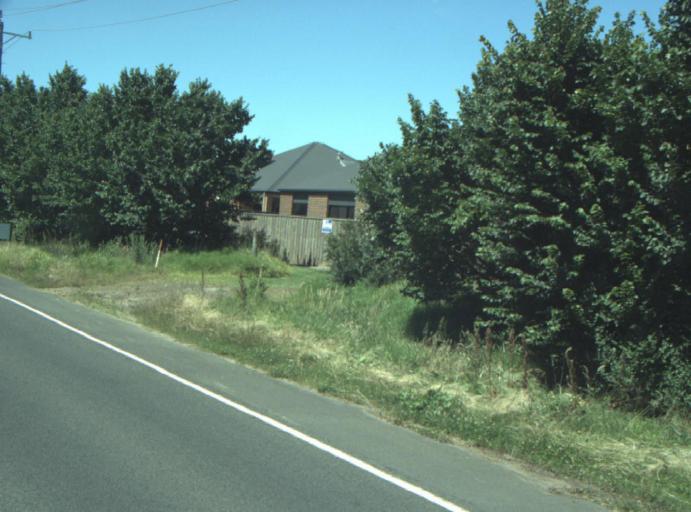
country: AU
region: Victoria
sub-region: Greater Geelong
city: Breakwater
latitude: -38.1934
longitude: 144.3596
